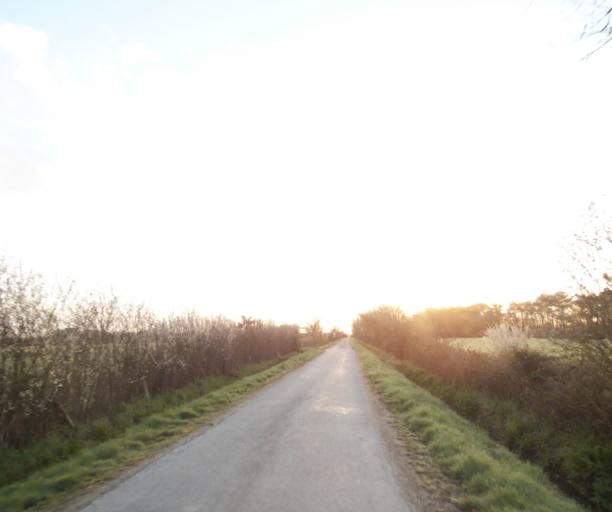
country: FR
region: Pays de la Loire
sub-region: Departement de la Loire-Atlantique
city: Quilly
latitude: 47.4408
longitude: -1.9157
